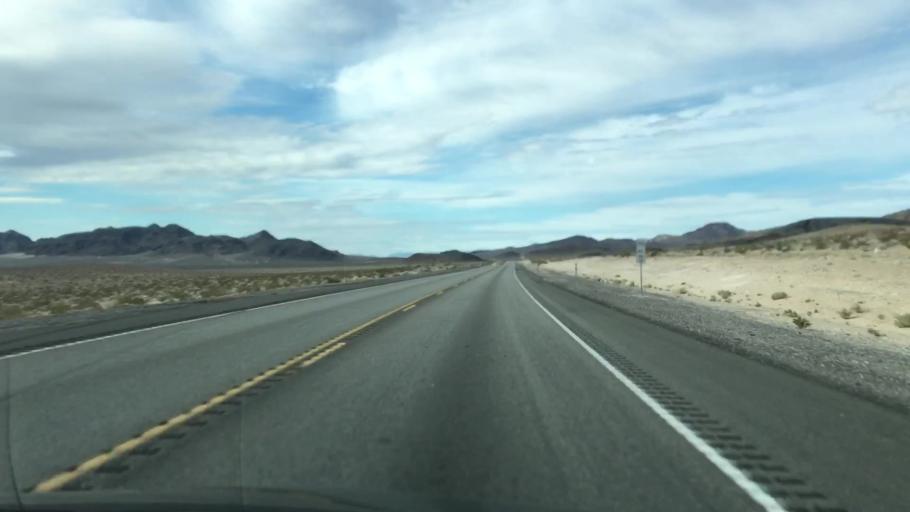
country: US
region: Nevada
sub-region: Nye County
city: Pahrump
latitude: 36.6128
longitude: -116.2759
